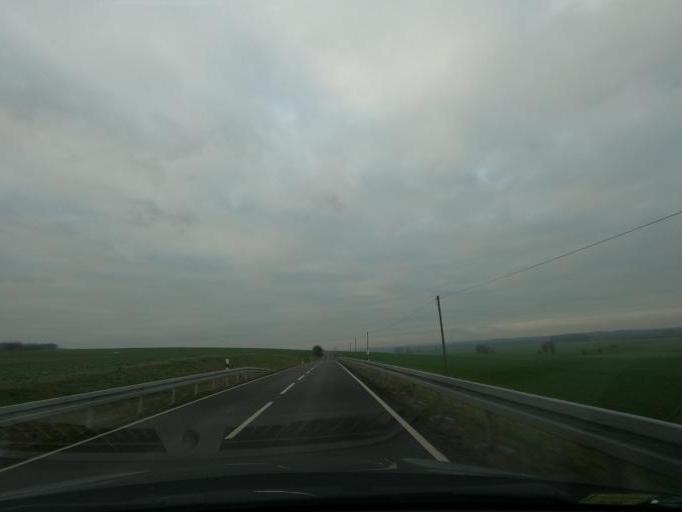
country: DE
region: Lower Saxony
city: Roklum
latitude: 52.0377
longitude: 10.7240
